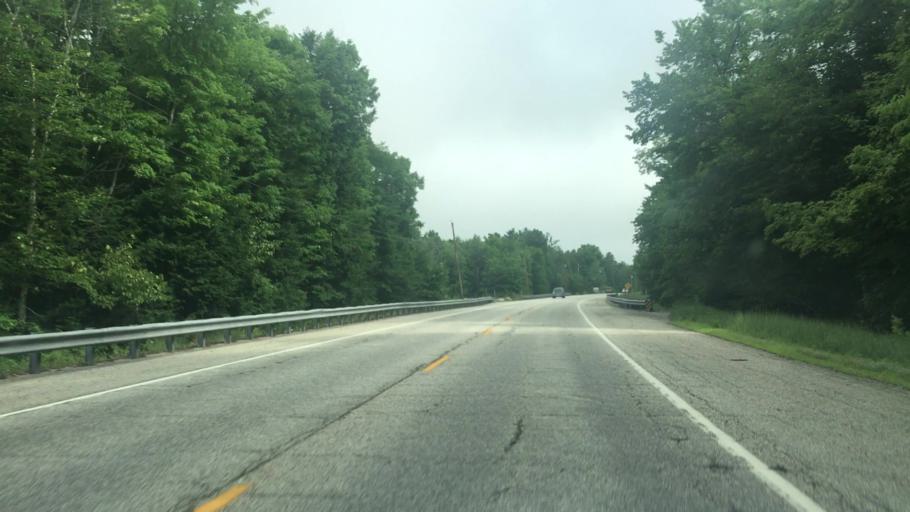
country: US
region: Maine
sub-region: Oxford County
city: Paris
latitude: 44.2613
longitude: -70.5149
